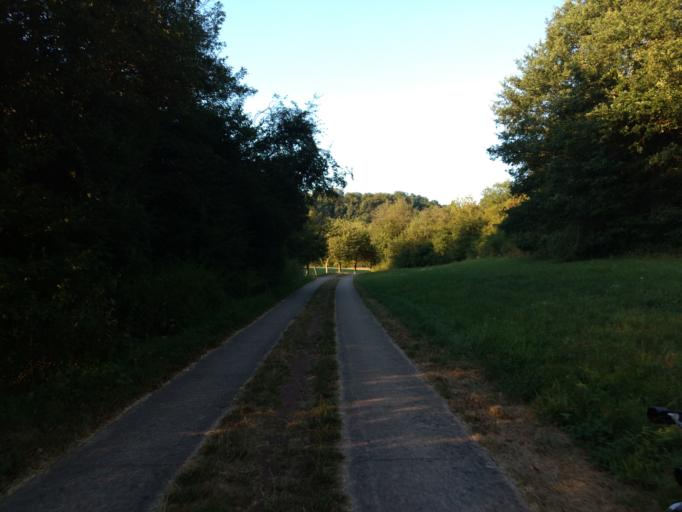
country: DE
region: Saarland
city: Rehlingen-Siersburg
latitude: 49.3649
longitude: 6.6334
